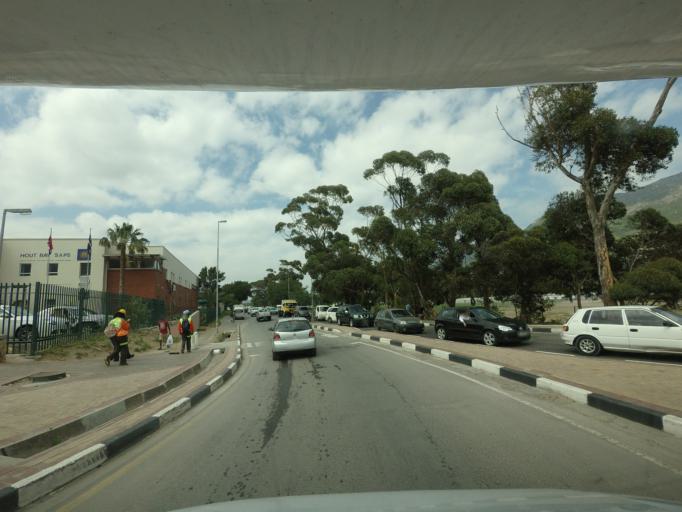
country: ZA
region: Western Cape
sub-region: City of Cape Town
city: Constantia
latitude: -34.0301
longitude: 18.3566
